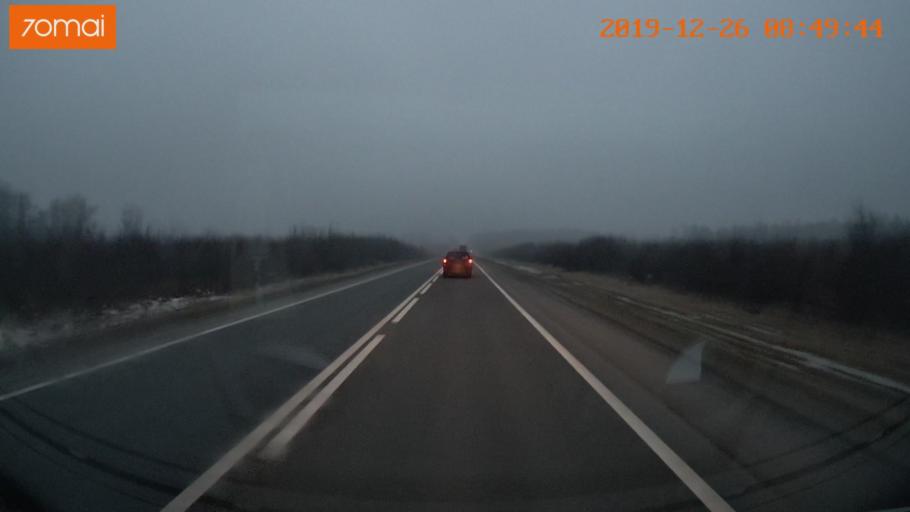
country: RU
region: Jaroslavl
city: Prechistoye
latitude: 58.6517
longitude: 40.3191
